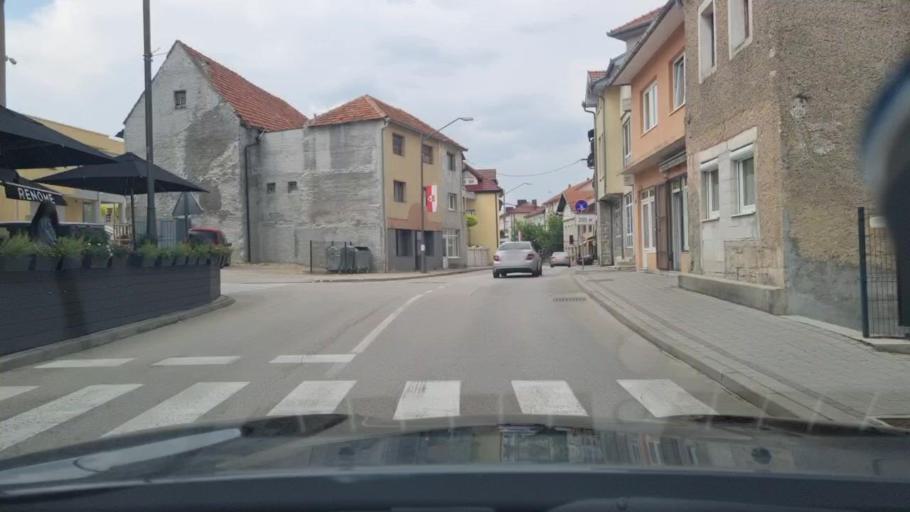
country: BA
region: Federation of Bosnia and Herzegovina
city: Tomislavgrad
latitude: 43.7186
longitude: 17.2261
